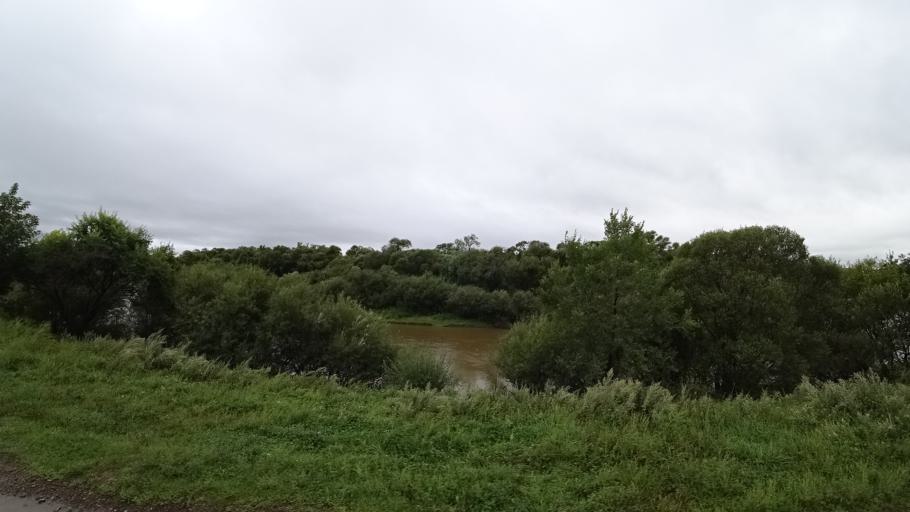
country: RU
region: Primorskiy
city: Monastyrishche
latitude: 44.2737
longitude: 132.4058
